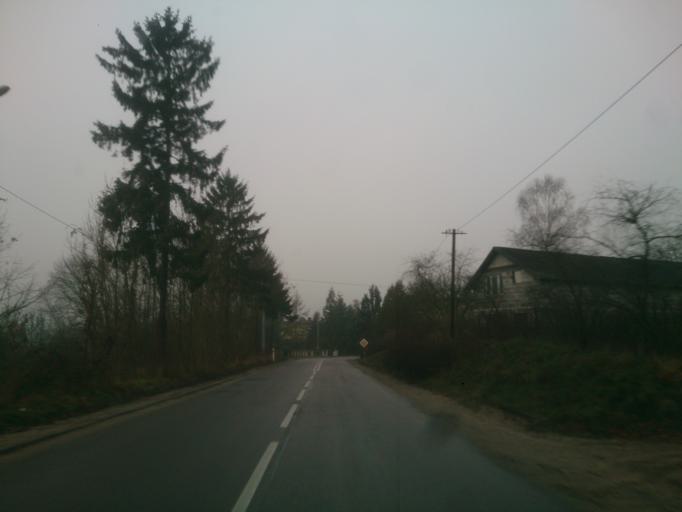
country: PL
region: Pomeranian Voivodeship
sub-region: Powiat starogardzki
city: Lubichowo
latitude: 53.8846
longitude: 18.3533
